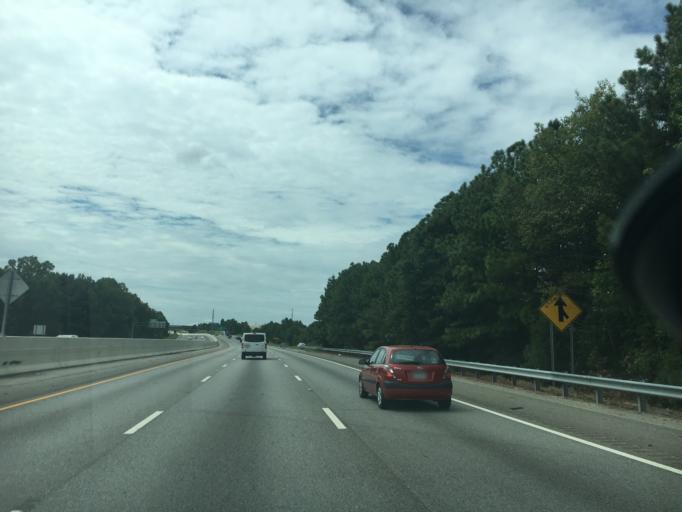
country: US
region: South Carolina
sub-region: Greenville County
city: Mauldin
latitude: 34.7639
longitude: -82.2799
